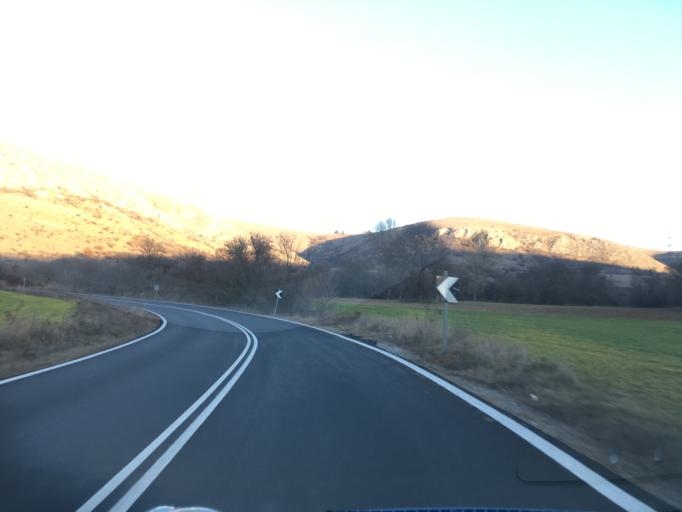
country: GR
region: West Macedonia
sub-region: Nomos Kozanis
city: Kozani
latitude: 40.3152
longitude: 21.7586
